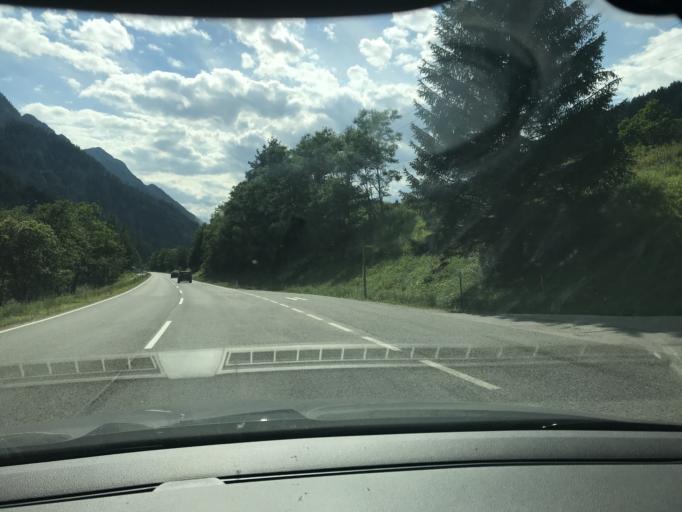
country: AT
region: Tyrol
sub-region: Politischer Bezirk Lienz
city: Leisach
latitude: 46.7915
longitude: 12.7092
